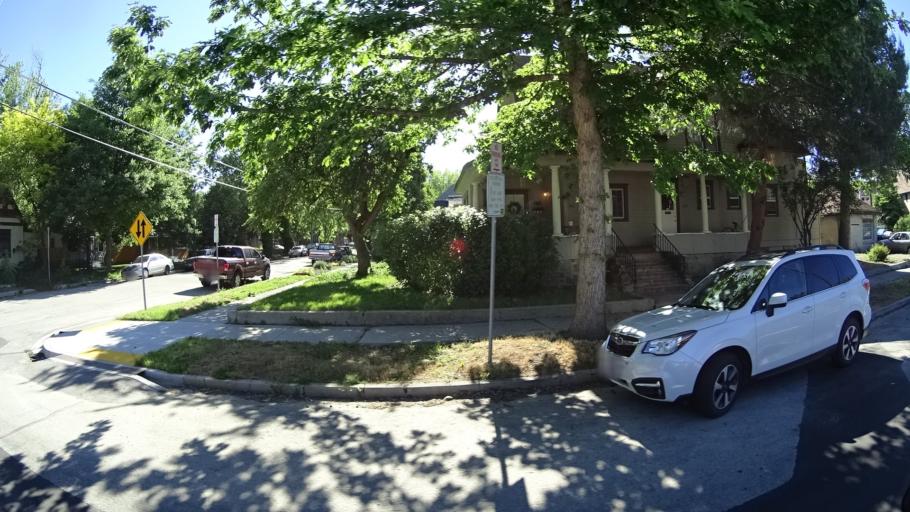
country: US
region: Idaho
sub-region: Ada County
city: Boise
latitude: 43.6248
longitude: -116.2022
